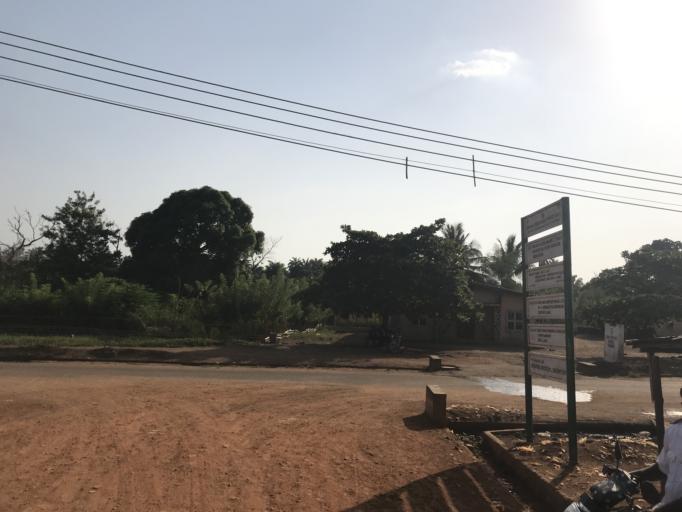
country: NG
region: Osun
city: Awo
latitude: 7.7525
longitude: 4.3172
